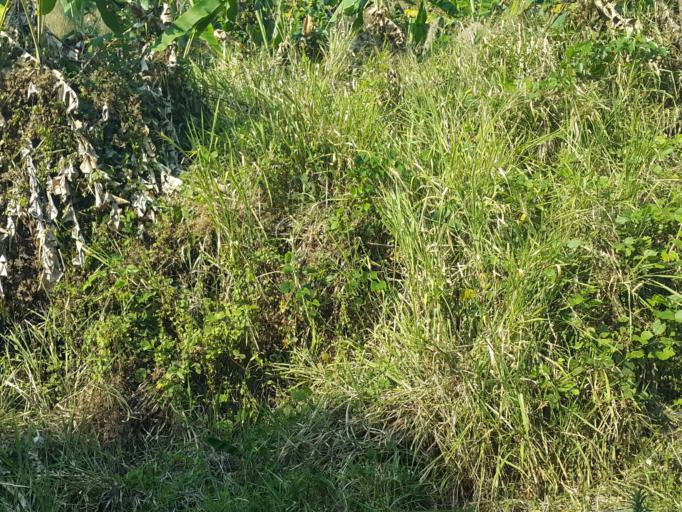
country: TH
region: Chiang Mai
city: Samoeng
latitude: 18.9017
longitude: 98.7932
